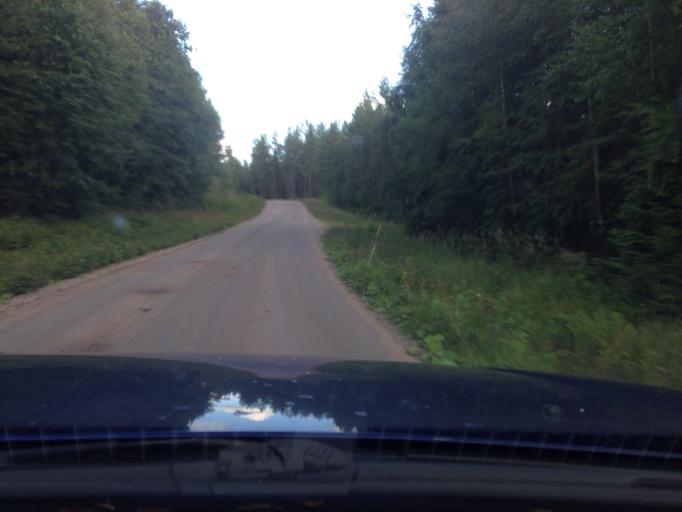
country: SE
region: Dalarna
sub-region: Vansbro Kommun
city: Jarna
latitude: 60.3289
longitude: 14.5603
